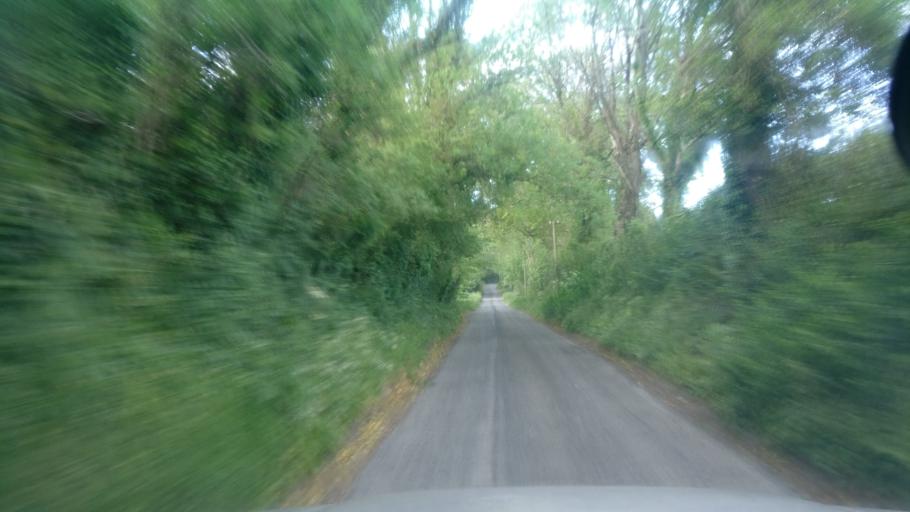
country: IE
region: Connaught
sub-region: County Galway
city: Ballinasloe
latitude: 53.2363
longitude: -8.2304
